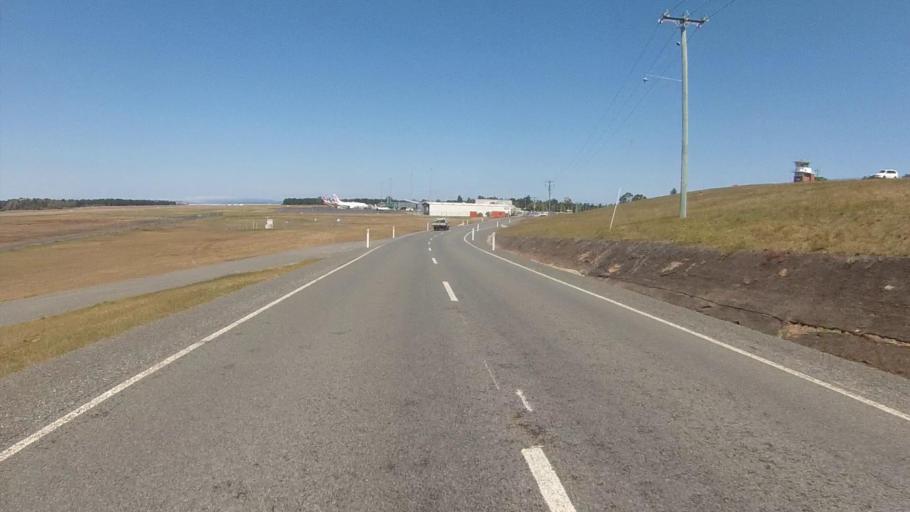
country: AU
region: Tasmania
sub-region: Clarence
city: Seven Mile Beach
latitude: -42.8331
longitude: 147.5019
